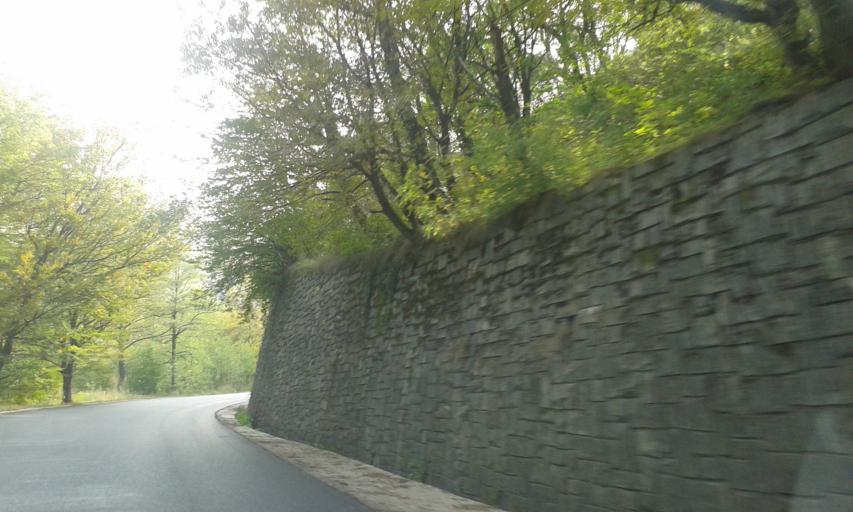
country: RO
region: Gorj
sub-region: Comuna Bumbesti-Jiu
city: Bumbesti-Jiu
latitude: 45.2706
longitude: 23.3842
